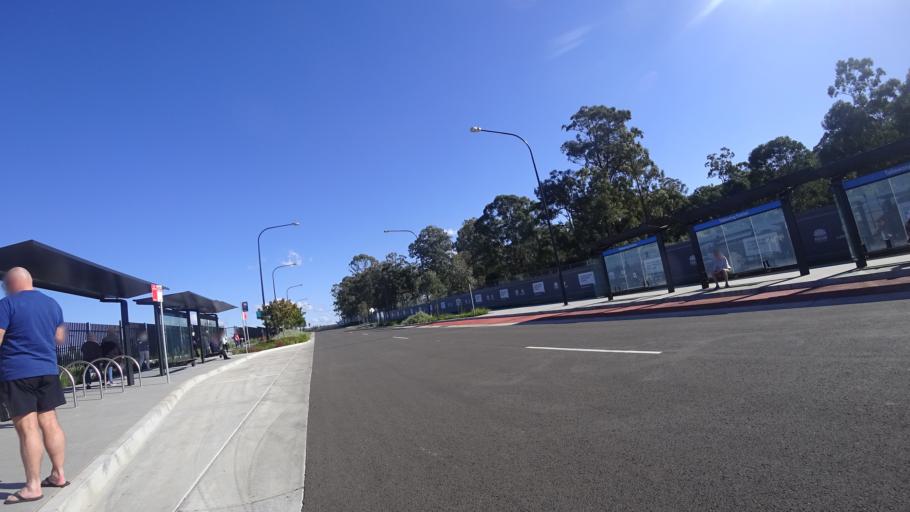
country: AU
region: New South Wales
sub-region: Blacktown
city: Rouse Hill
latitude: -33.6914
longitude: 150.9057
